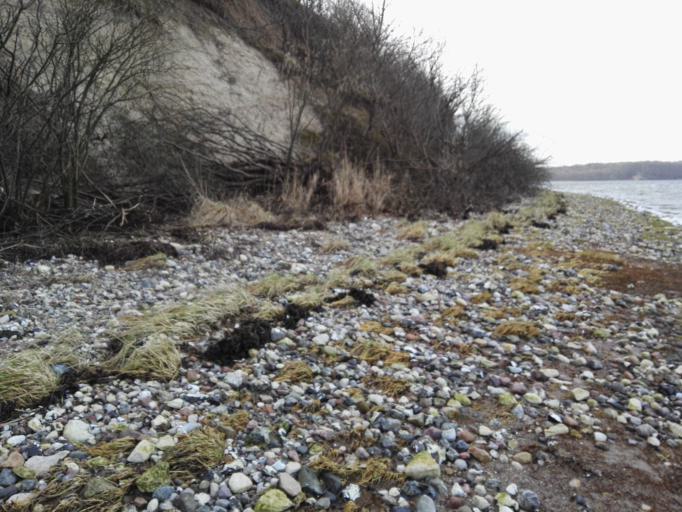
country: DK
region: Capital Region
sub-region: Frederikssund Kommune
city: Frederikssund
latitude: 55.8586
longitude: 12.0482
